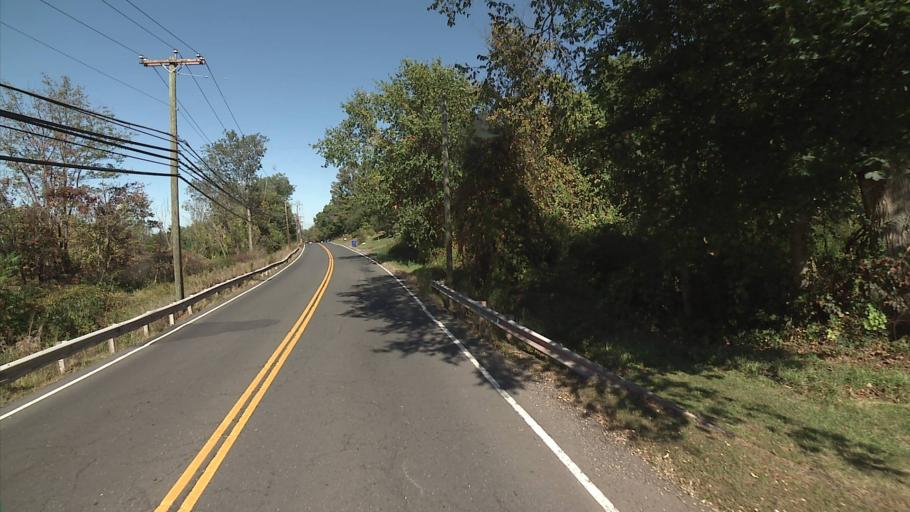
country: US
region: Connecticut
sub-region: Tolland County
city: Ellington
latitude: 41.9060
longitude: -72.4558
